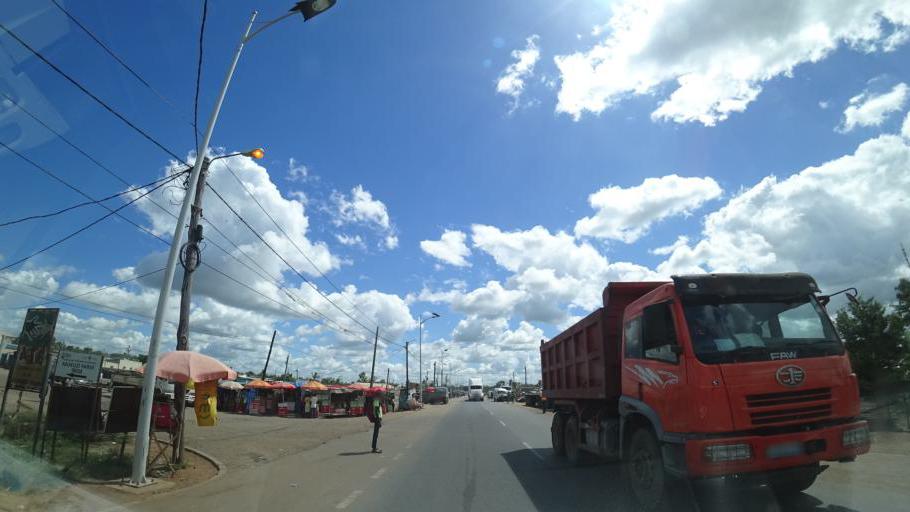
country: MZ
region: Sofala
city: Dondo
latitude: -19.2703
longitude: 34.2094
